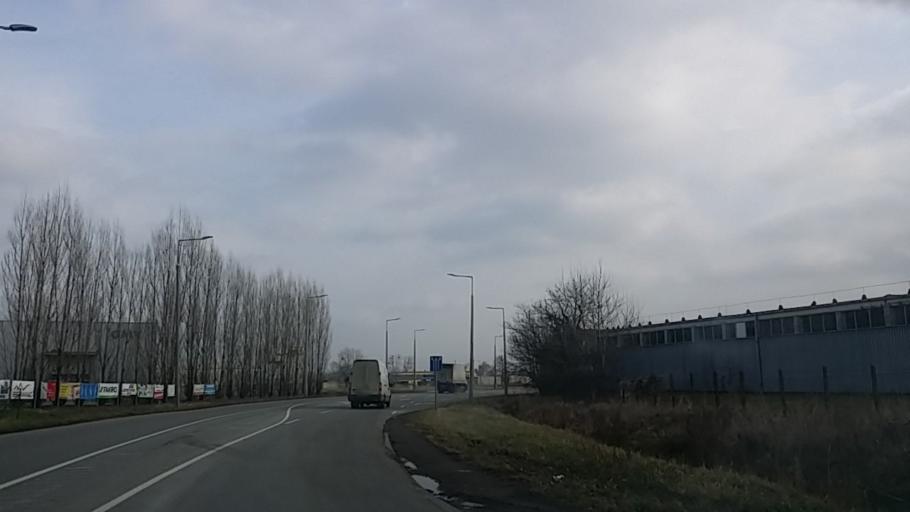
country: HU
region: Tolna
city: Szekszard
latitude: 46.3559
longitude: 18.7194
